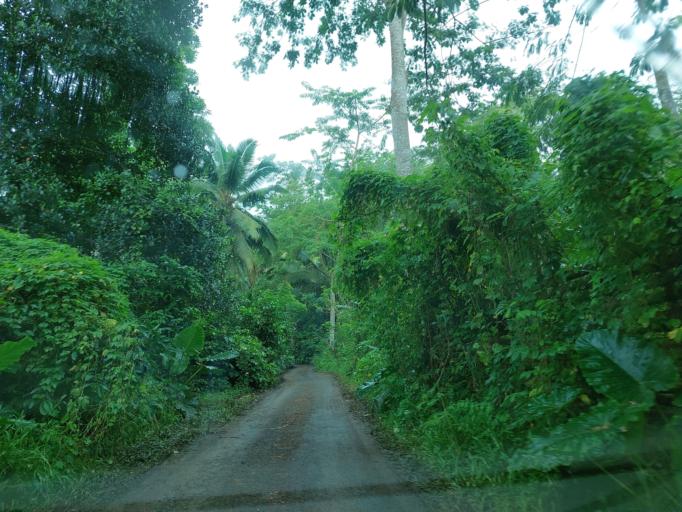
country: YT
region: Tsingoni
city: Tsingoni
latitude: -12.7668
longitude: 45.1210
